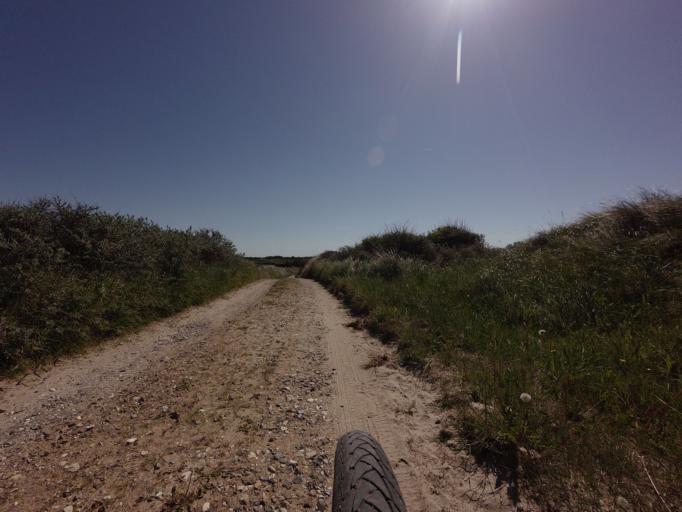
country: DK
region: North Denmark
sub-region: Jammerbugt Kommune
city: Pandrup
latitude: 57.3050
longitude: 9.6484
